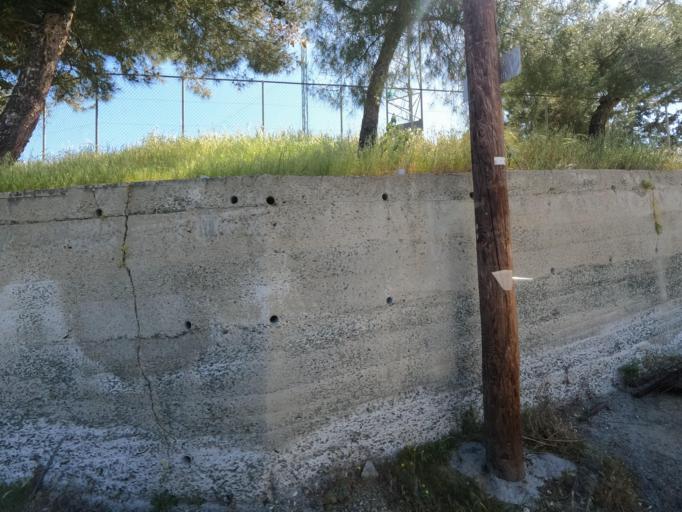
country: CY
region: Lefkosia
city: Peristerona
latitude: 35.0502
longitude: 33.0559
